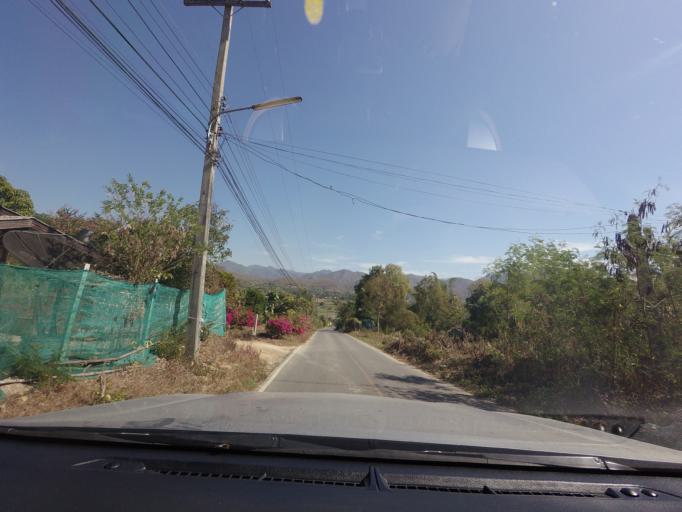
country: TH
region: Mae Hong Son
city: Wiang Nuea
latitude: 19.3858
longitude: 98.4378
